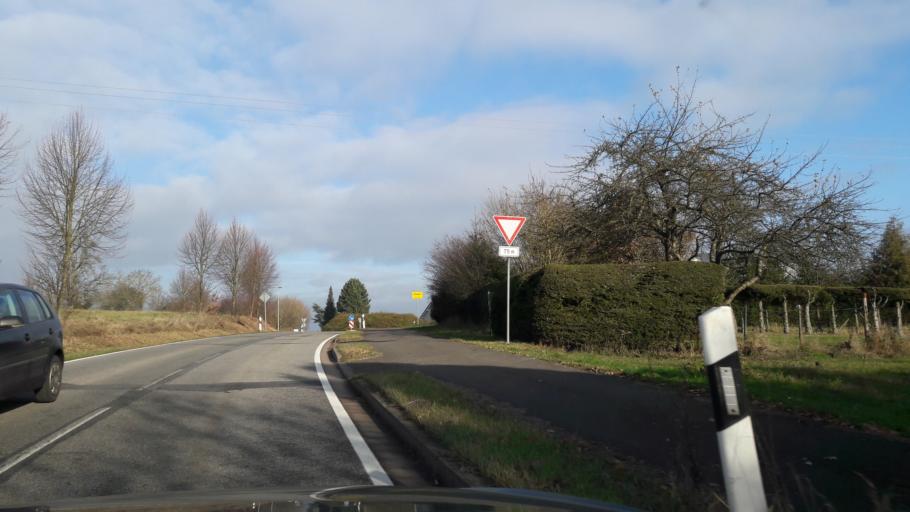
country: DE
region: Rheinland-Pfalz
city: Brucken
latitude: 49.4267
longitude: 7.3516
